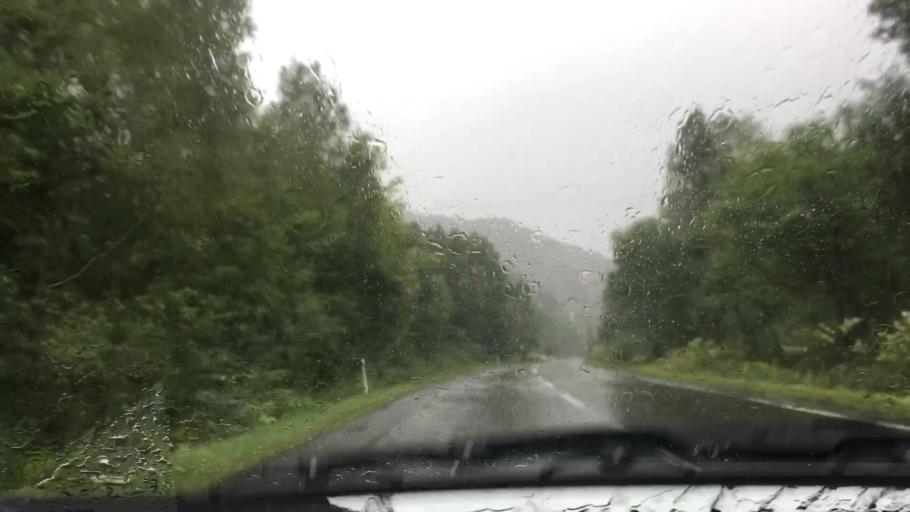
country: JP
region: Hokkaido
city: Sapporo
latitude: 42.9498
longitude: 141.1472
